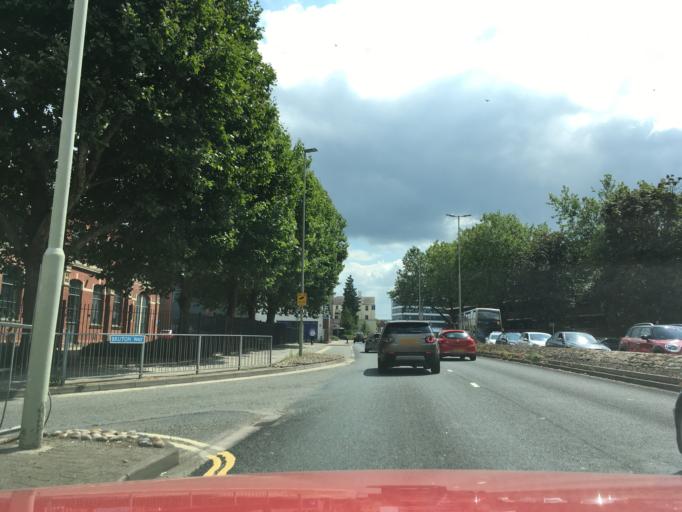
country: GB
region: England
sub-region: Gloucestershire
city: Gloucester
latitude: 51.8670
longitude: -2.2410
